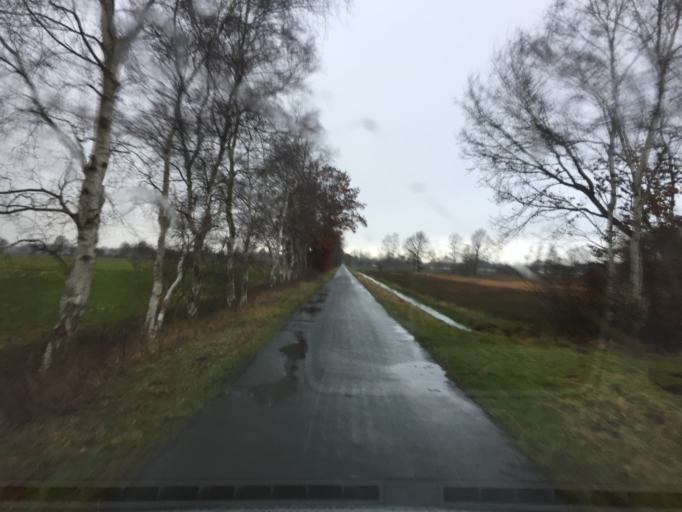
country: DE
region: Lower Saxony
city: Hassel
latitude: 52.6565
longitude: 8.8490
